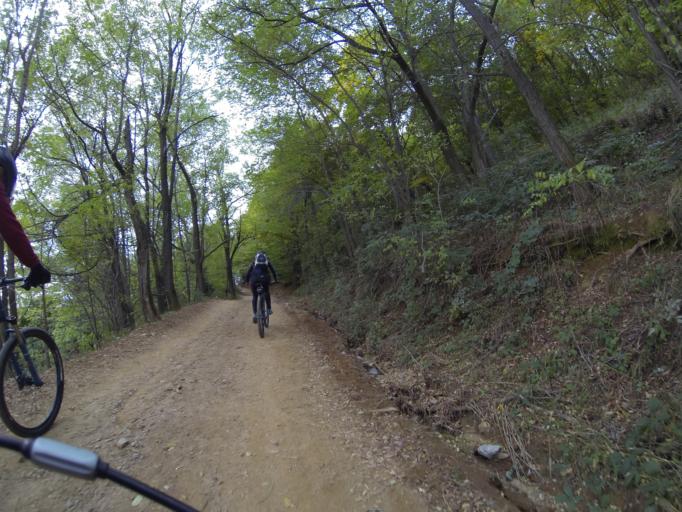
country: RO
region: Gorj
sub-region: Comuna Tismana
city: Sohodol
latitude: 45.0644
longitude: 22.8690
